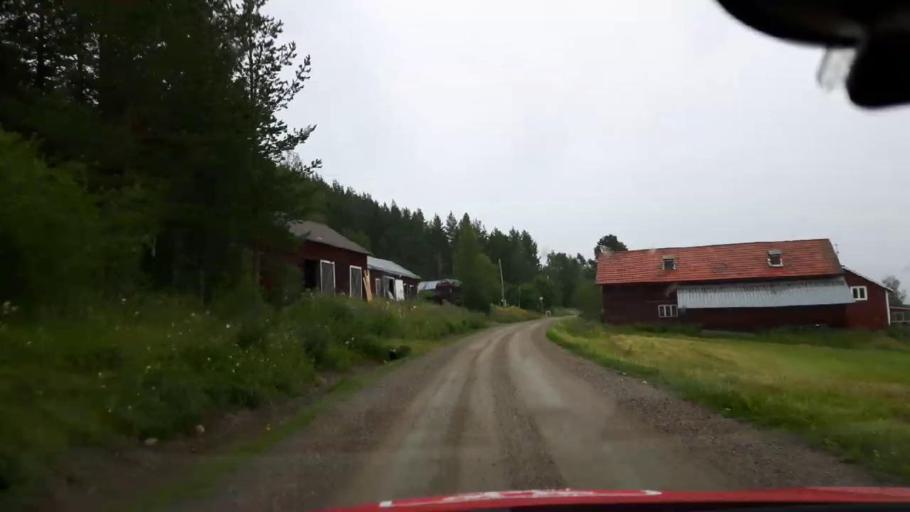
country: SE
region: Jaemtland
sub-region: OEstersunds Kommun
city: Brunflo
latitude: 62.8148
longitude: 14.8993
